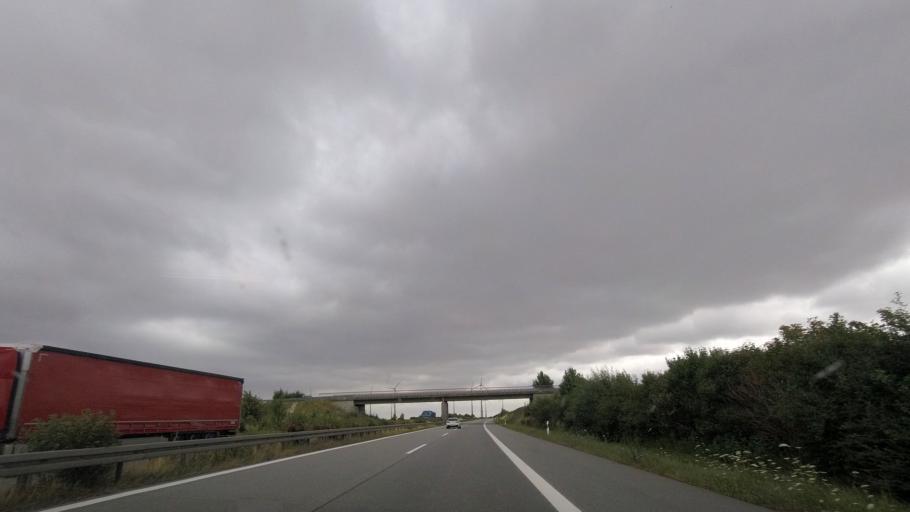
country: DE
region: Mecklenburg-Vorpommern
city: Gross Miltzow
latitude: 53.5599
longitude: 13.5136
